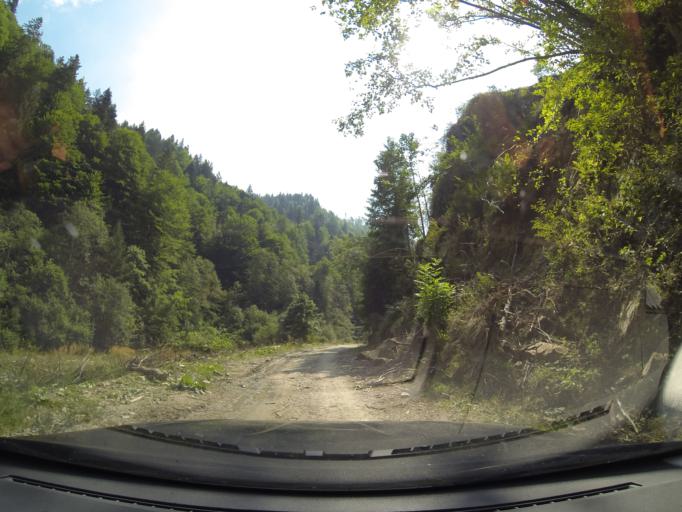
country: RO
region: Arges
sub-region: Comuna Arefu
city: Arefu
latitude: 45.4844
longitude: 24.6377
